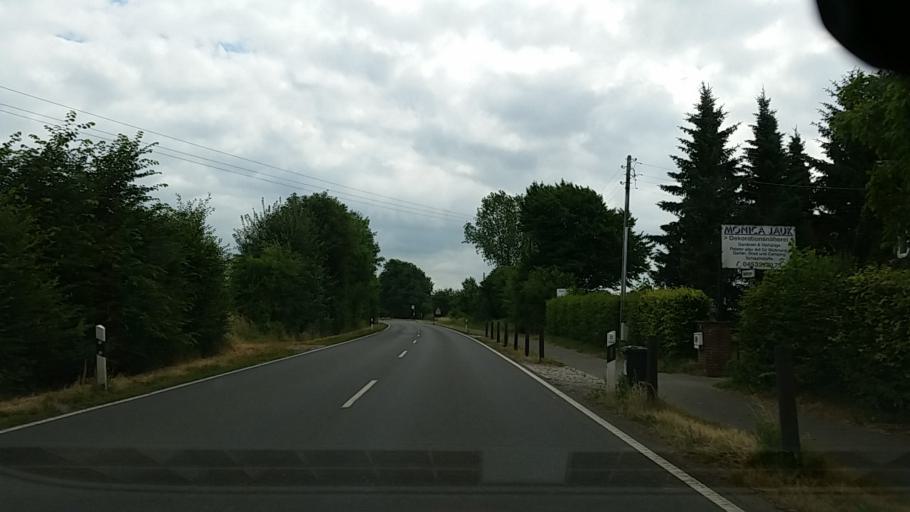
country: DE
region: Schleswig-Holstein
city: Bargfeld-Stegen
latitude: 53.7649
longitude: 10.2099
